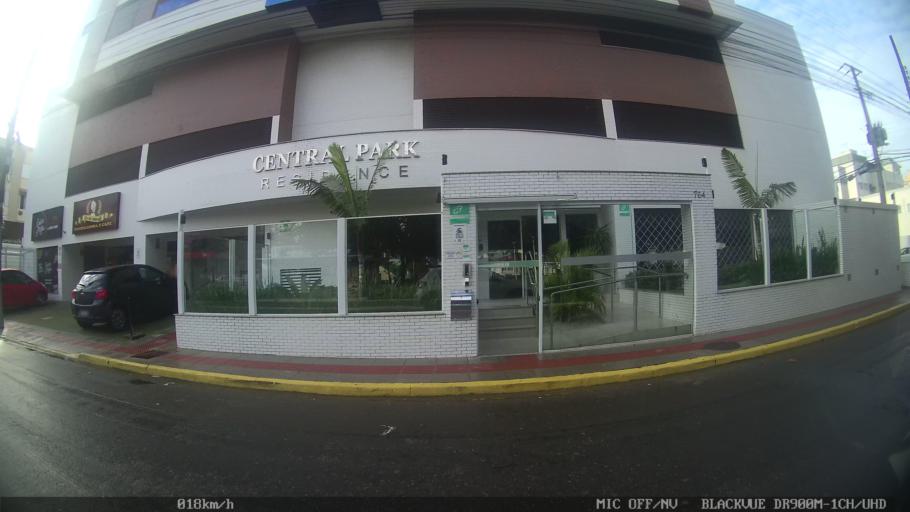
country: BR
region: Santa Catarina
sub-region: Sao Jose
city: Campinas
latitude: -27.5958
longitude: -48.6146
